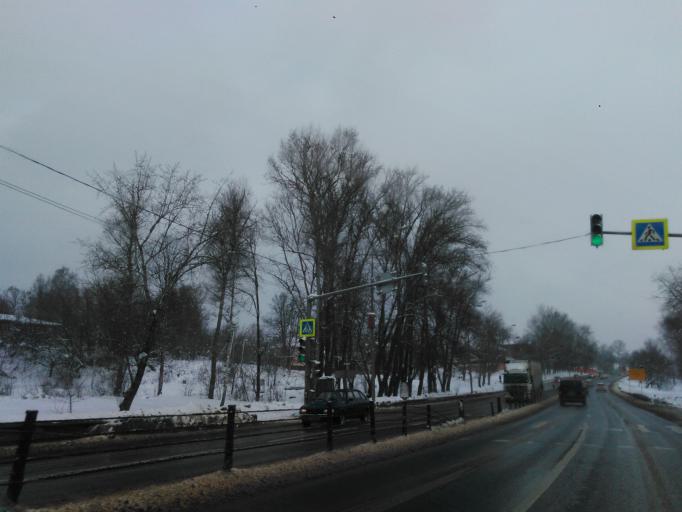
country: RU
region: Moskovskaya
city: Iksha
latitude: 56.1692
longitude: 37.5060
